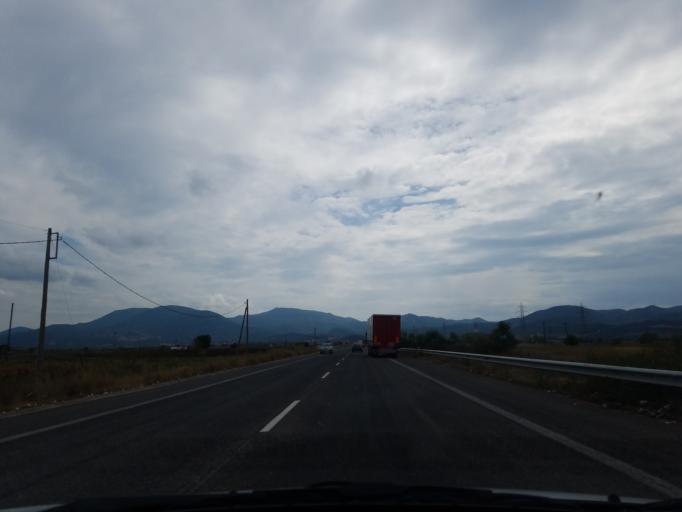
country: GR
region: Central Greece
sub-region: Nomos Fthiotidos
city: Domokos
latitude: 39.0489
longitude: 22.3453
